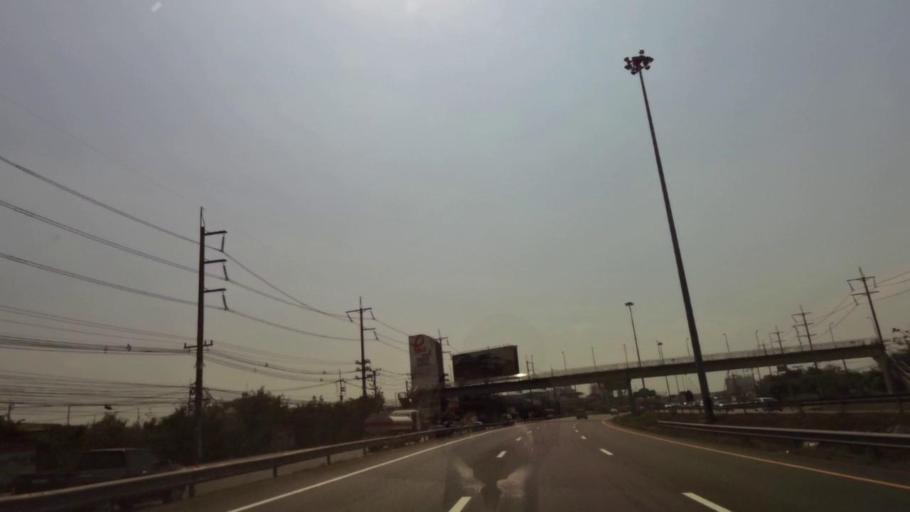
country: TH
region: Chon Buri
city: Chon Buri
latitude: 13.4267
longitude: 101.0033
